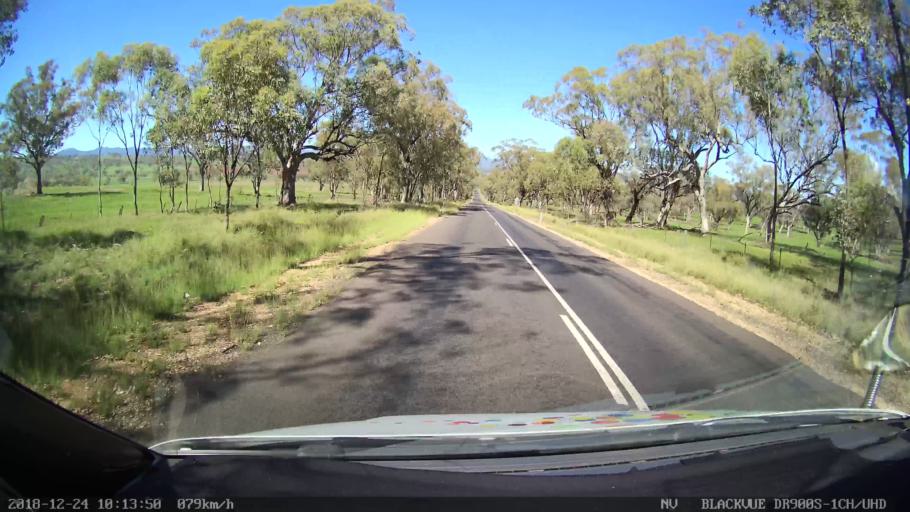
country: AU
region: New South Wales
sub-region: Liverpool Plains
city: Quirindi
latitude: -31.6933
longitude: 150.6365
